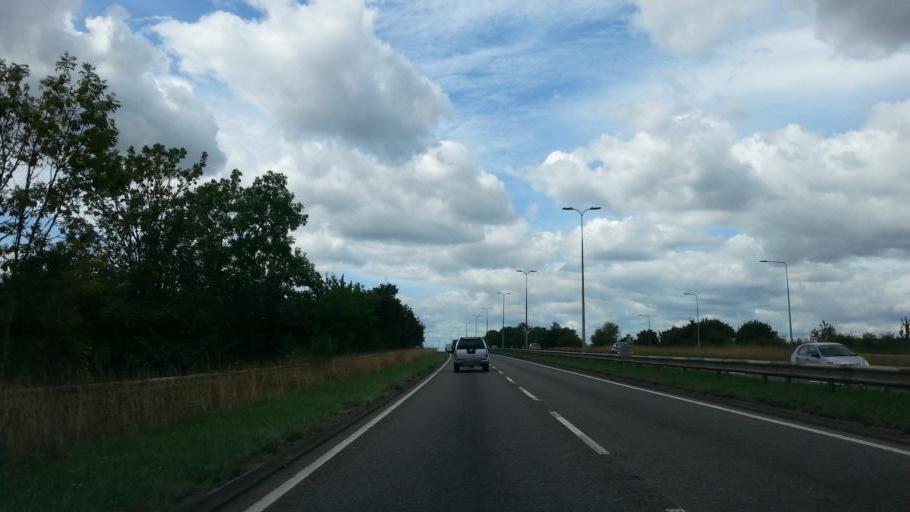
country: GB
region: England
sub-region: Essex
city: Wickford
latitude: 51.5924
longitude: 0.5042
